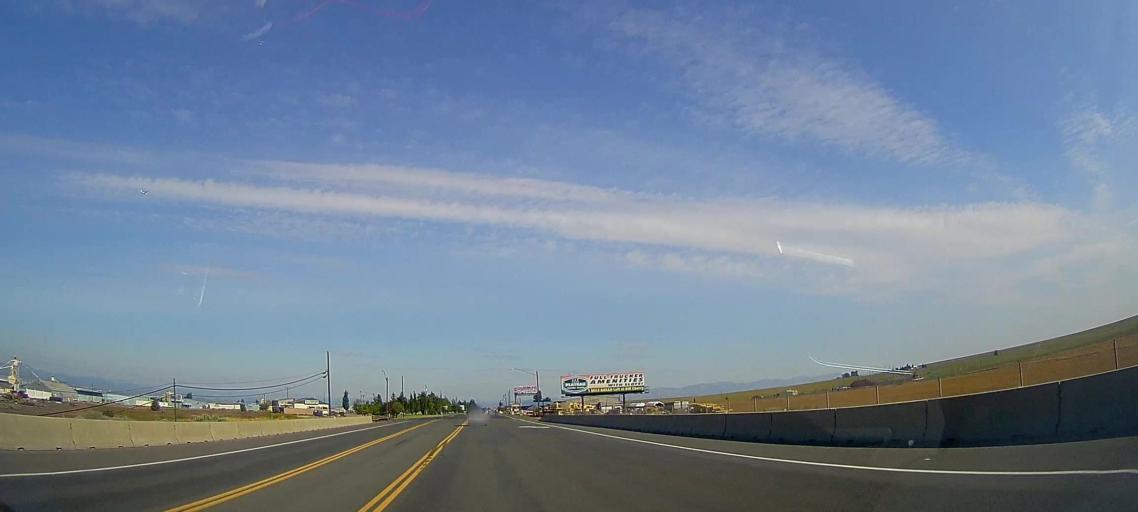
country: US
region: Oregon
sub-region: Jefferson County
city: Madras
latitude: 44.6565
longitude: -121.1300
